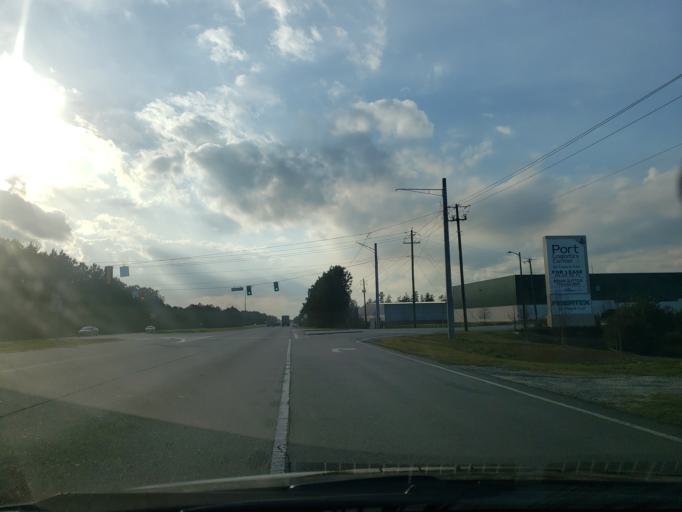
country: US
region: Georgia
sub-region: Chatham County
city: Pooler
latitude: 32.1630
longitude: -81.2414
